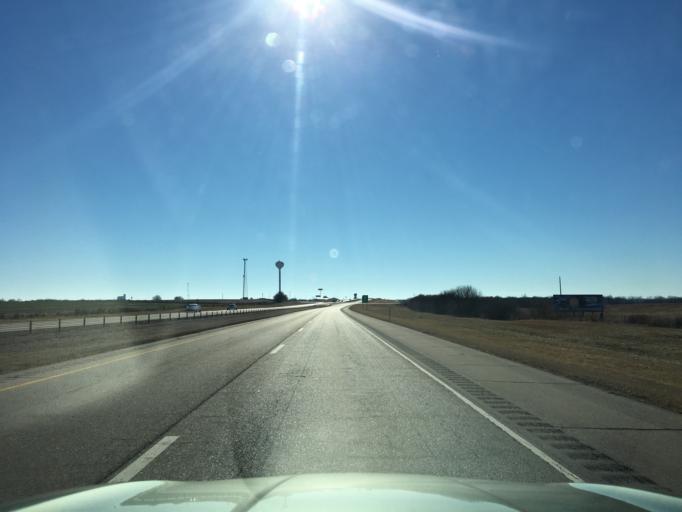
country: US
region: Oklahoma
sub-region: Kay County
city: Blackwell
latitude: 36.9492
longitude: -97.3458
